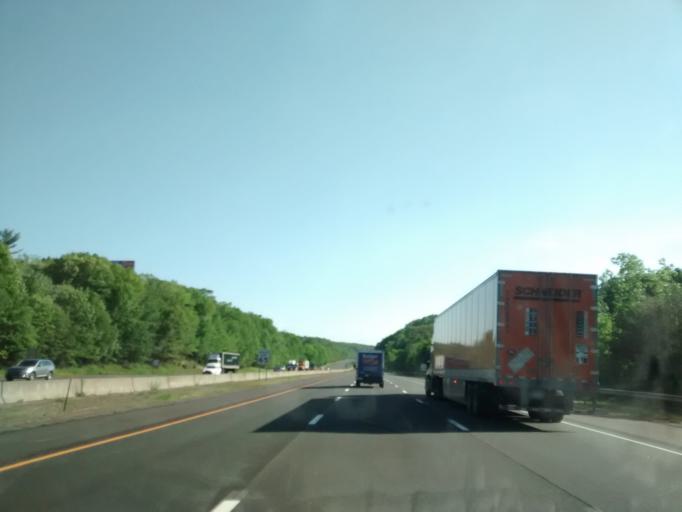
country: US
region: Connecticut
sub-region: Tolland County
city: Stafford Springs
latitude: 41.9202
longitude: -72.2626
